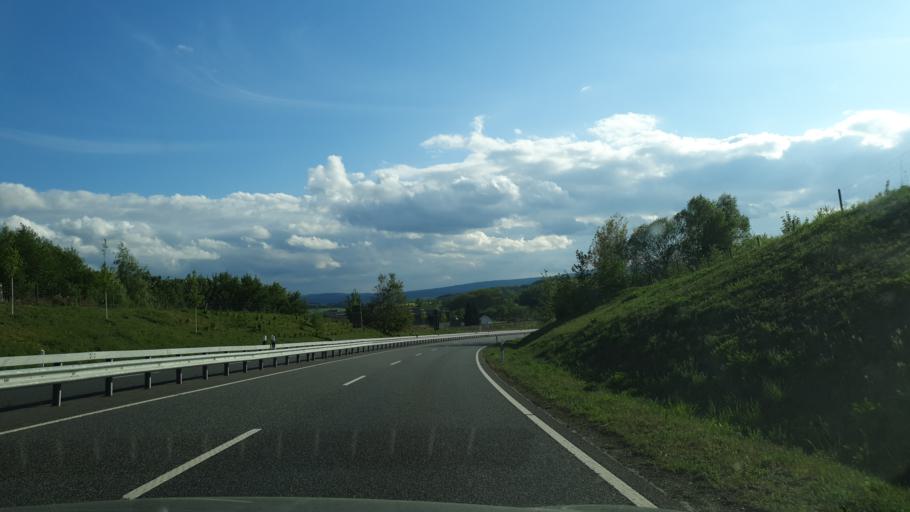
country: DE
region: Rheinland-Pfalz
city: Oberahr
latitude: 50.4898
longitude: 7.8707
